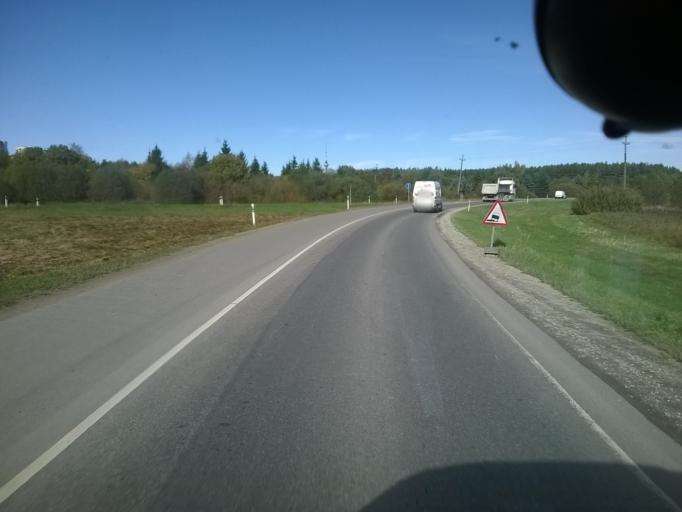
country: EE
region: Harju
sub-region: Tallinna linn
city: Kose
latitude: 59.4410
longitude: 24.9103
